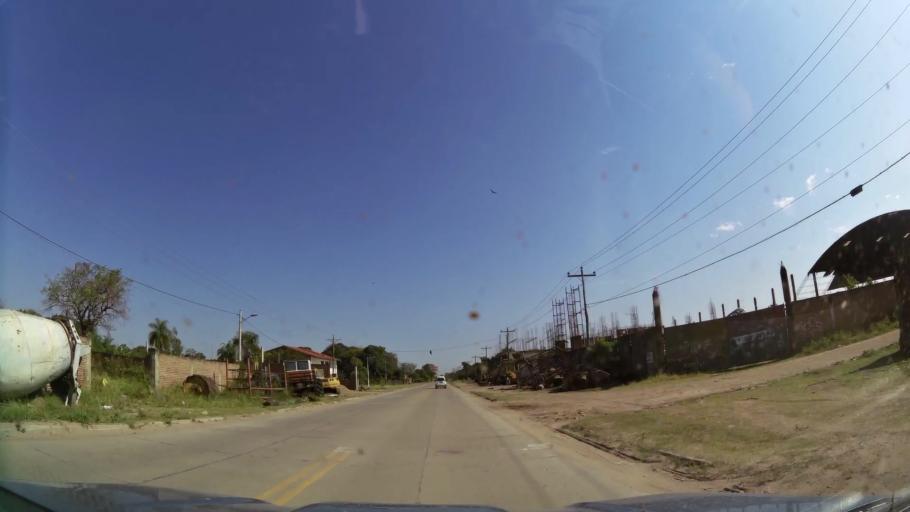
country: BO
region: Santa Cruz
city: Santa Cruz de la Sierra
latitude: -17.7609
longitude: -63.1100
